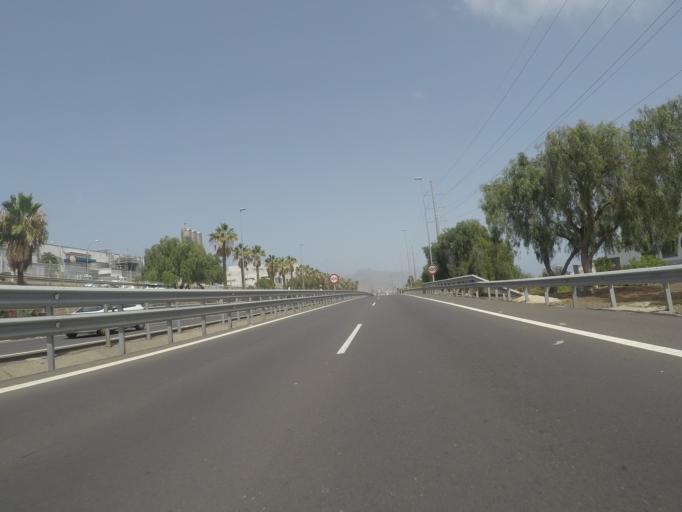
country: ES
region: Canary Islands
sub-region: Provincia de Santa Cruz de Tenerife
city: Santa Cruz de Tenerife
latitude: 28.4468
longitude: -16.2748
